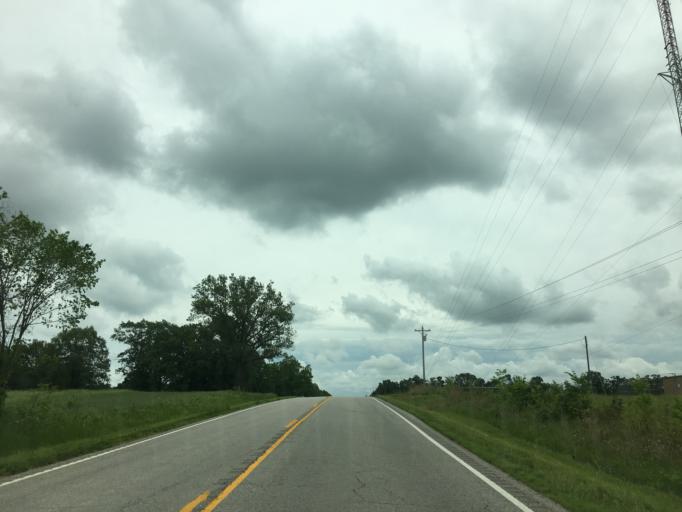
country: US
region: Missouri
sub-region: Gasconade County
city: Owensville
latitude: 38.4904
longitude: -91.4620
